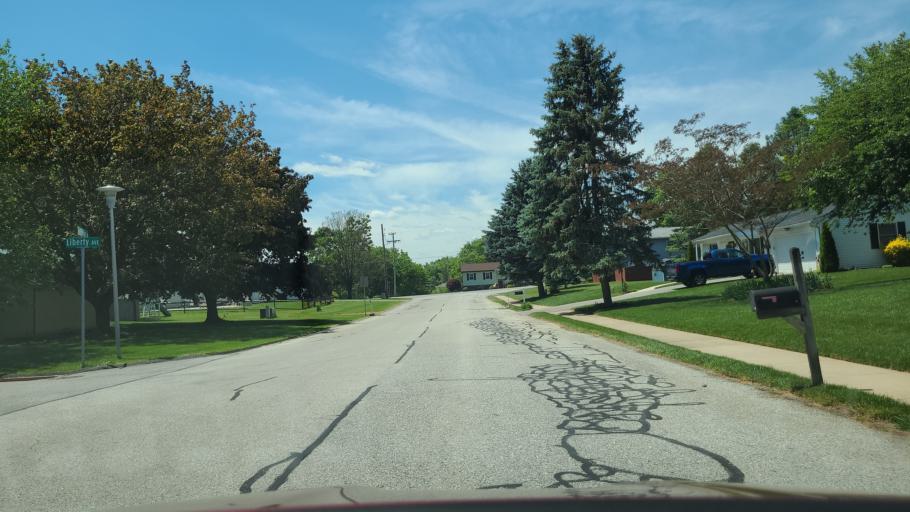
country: US
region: Pennsylvania
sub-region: York County
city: New Freedom
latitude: 39.7359
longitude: -76.6916
